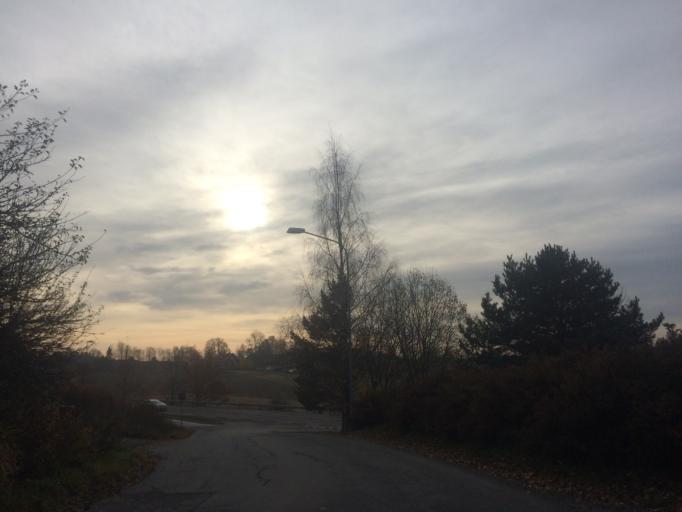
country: NO
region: Akershus
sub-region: Ski
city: Ski
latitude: 59.7252
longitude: 10.8427
